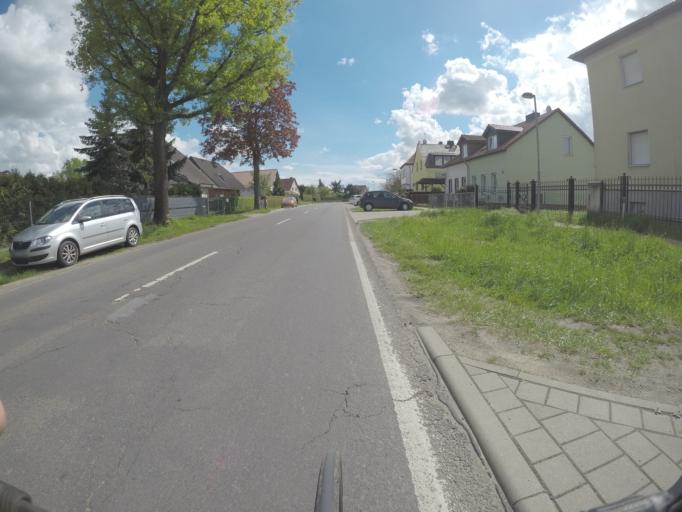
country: DE
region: Brandenburg
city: Bernau bei Berlin
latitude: 52.6899
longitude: 13.5882
